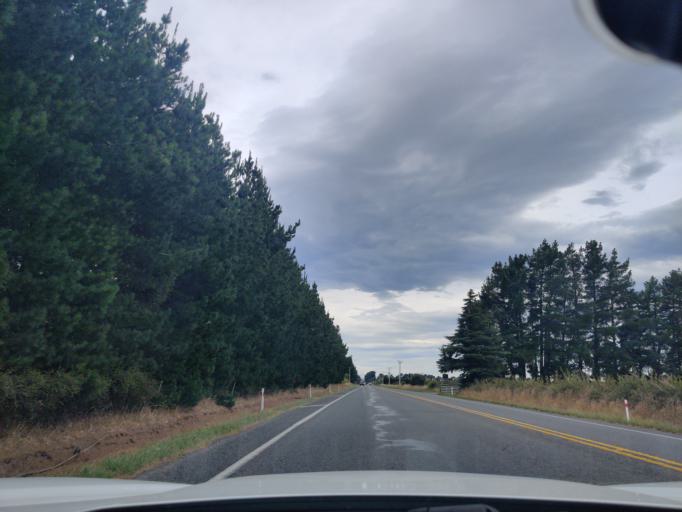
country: NZ
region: Wellington
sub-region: Masterton District
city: Masterton
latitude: -40.9917
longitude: 175.5695
